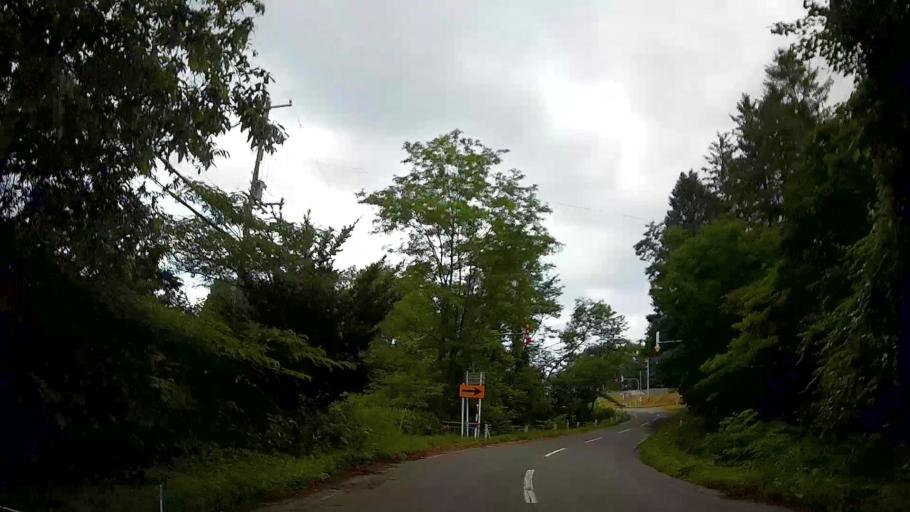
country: JP
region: Hokkaido
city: Nanae
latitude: 42.0969
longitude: 140.5598
